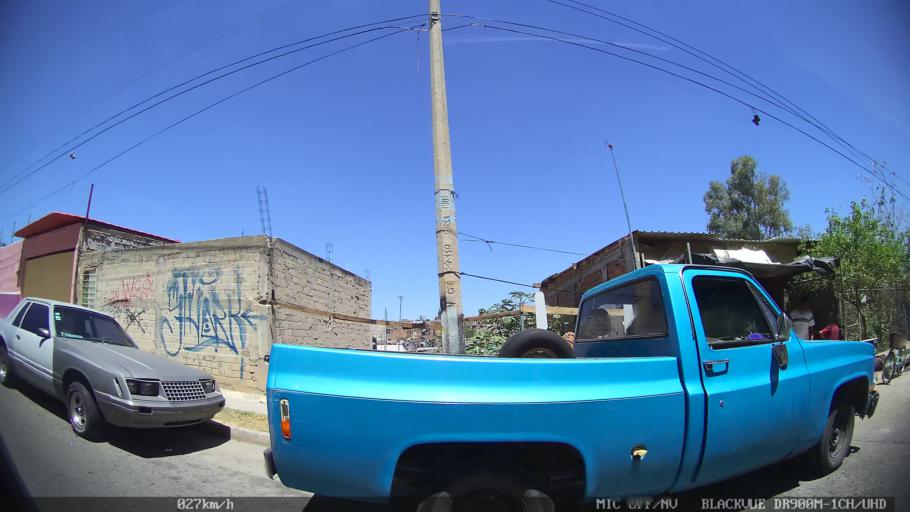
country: MX
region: Jalisco
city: Tlaquepaque
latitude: 20.6833
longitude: -103.2896
